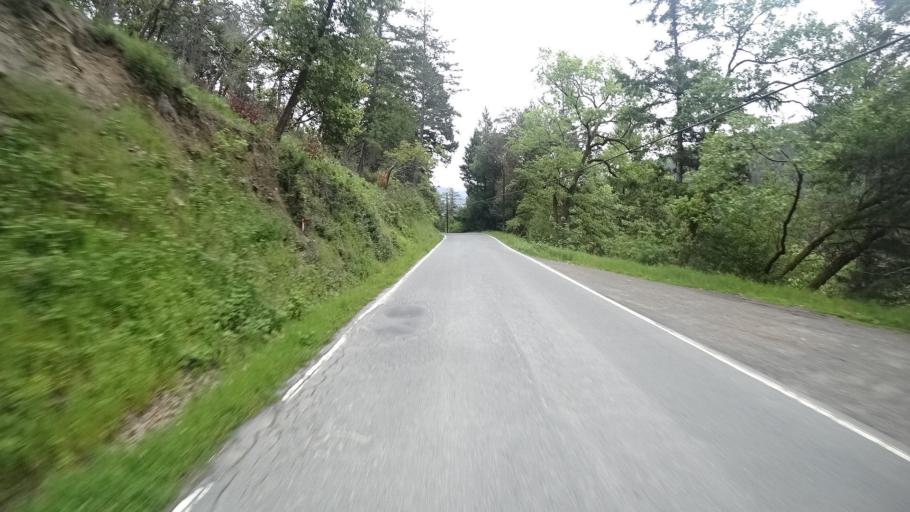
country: US
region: California
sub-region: Humboldt County
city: Willow Creek
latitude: 41.1984
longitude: -123.7339
